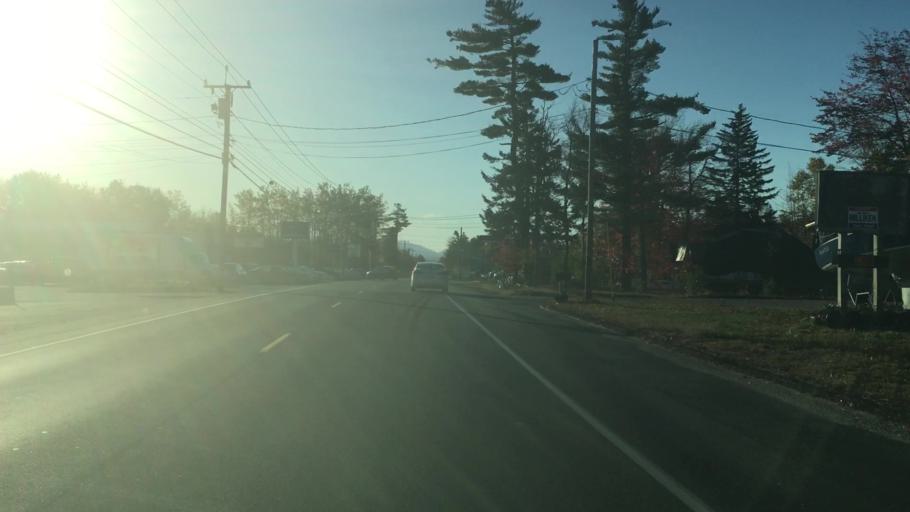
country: US
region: Maine
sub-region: Hancock County
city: Ellsworth
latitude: 44.5096
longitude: -68.3908
